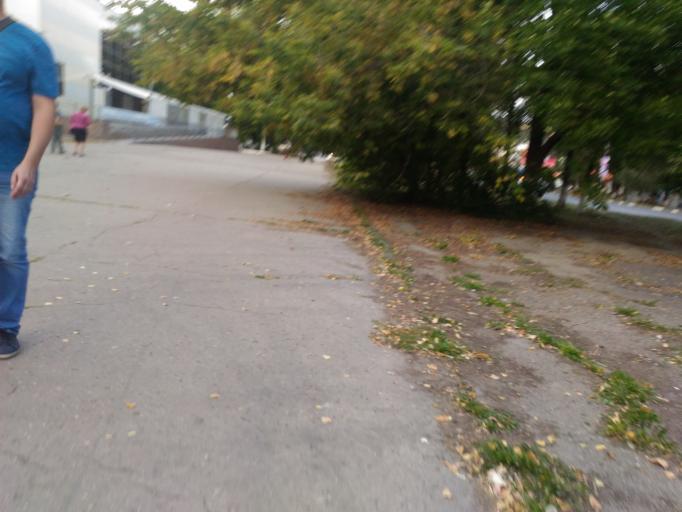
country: RU
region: Ulyanovsk
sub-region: Ulyanovskiy Rayon
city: Ulyanovsk
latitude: 54.3024
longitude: 48.3302
